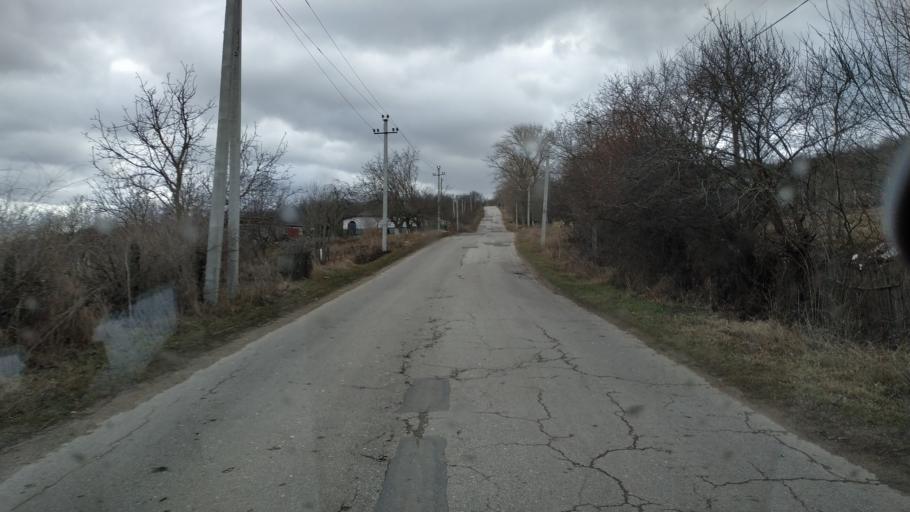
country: MD
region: Stinga Nistrului
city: Bucovat
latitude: 47.2263
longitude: 28.4262
